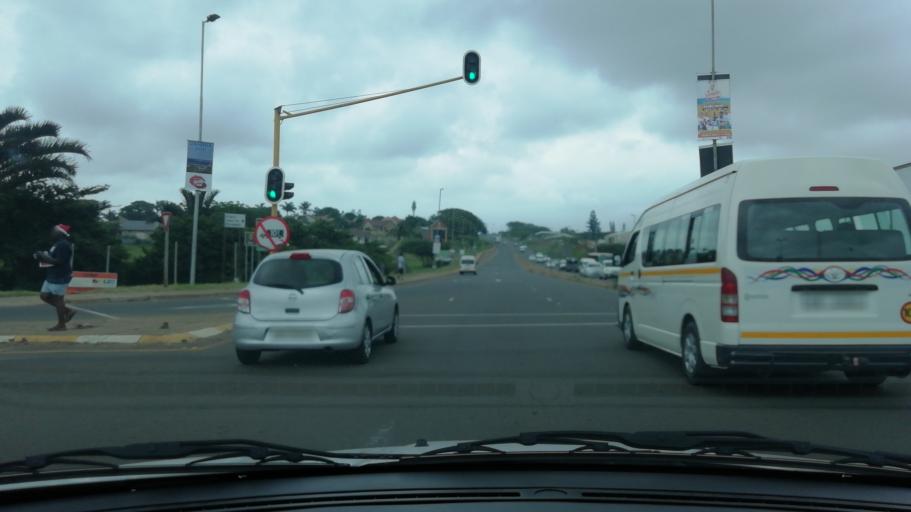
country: ZA
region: KwaZulu-Natal
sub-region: uThungulu District Municipality
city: Empangeni
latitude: -28.7639
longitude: 31.9072
